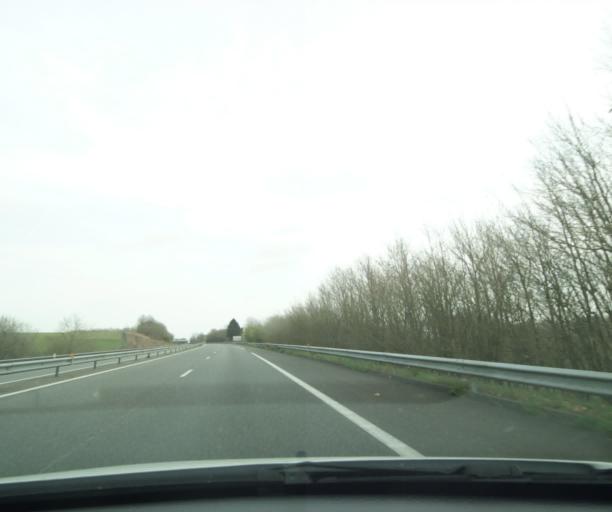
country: FR
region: Aquitaine
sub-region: Departement des Landes
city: Peyrehorade
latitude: 43.5155
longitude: -1.1233
